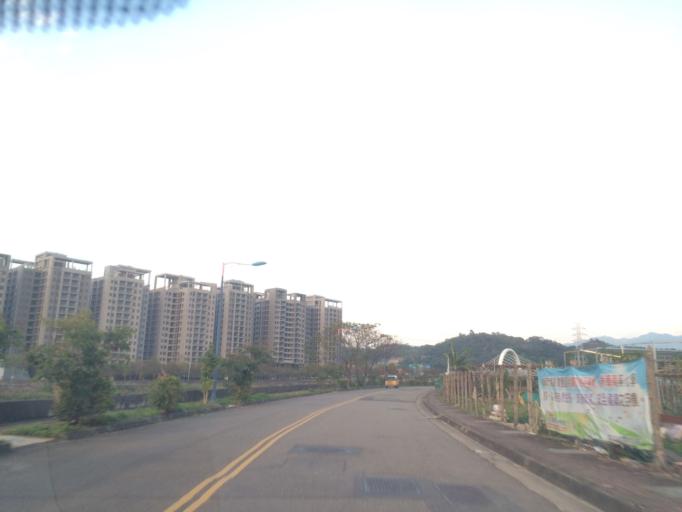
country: TW
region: Taiwan
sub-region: Taichung City
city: Taichung
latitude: 24.1589
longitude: 120.7300
